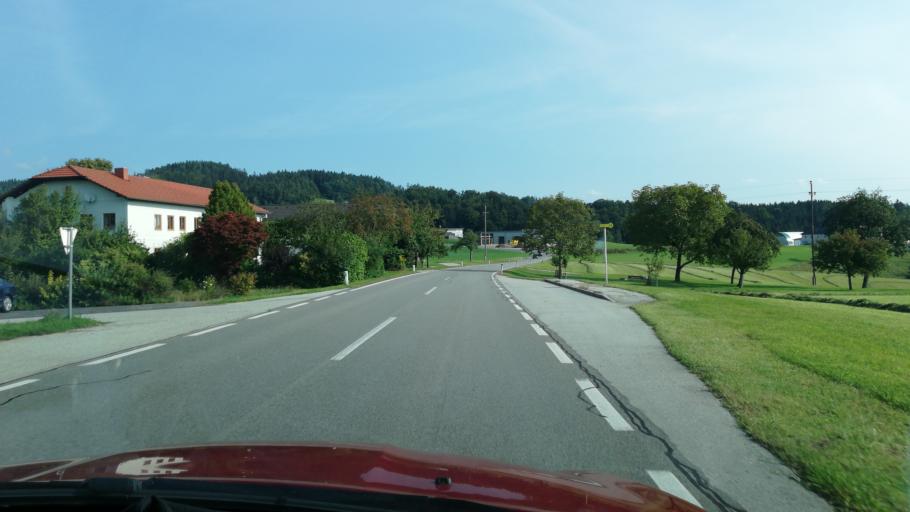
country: AT
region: Upper Austria
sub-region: Politischer Bezirk Perg
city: Perg
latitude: 48.3808
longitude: 14.7043
